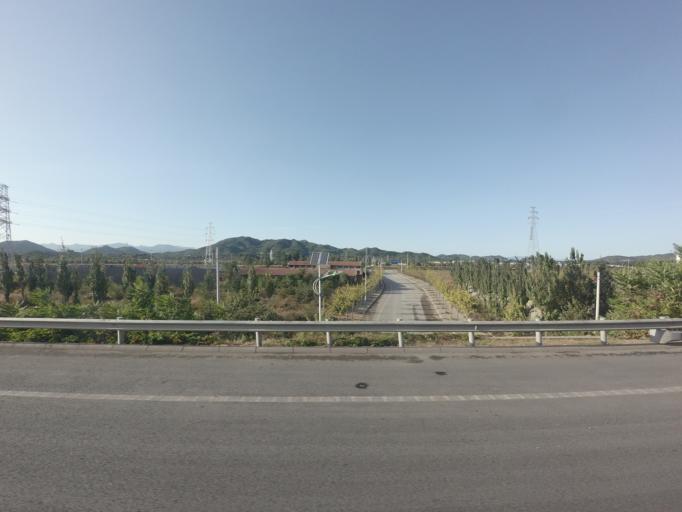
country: CN
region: Beijing
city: Jugezhuang
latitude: 40.3944
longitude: 116.9243
